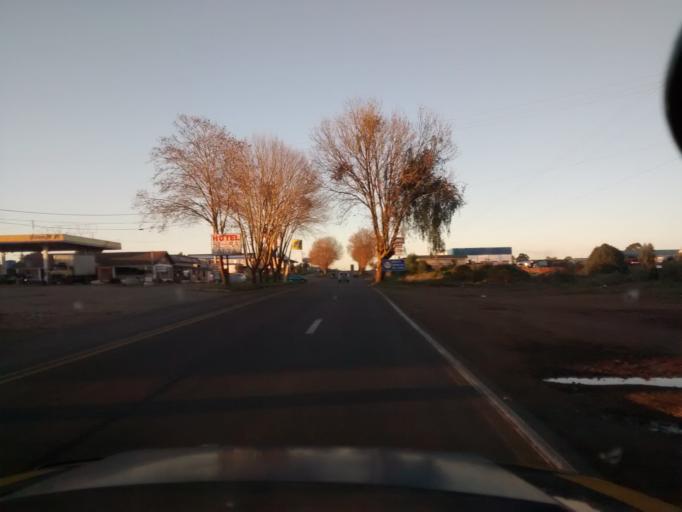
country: BR
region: Rio Grande do Sul
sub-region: Vacaria
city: Vacaria
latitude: -28.5246
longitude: -50.9462
